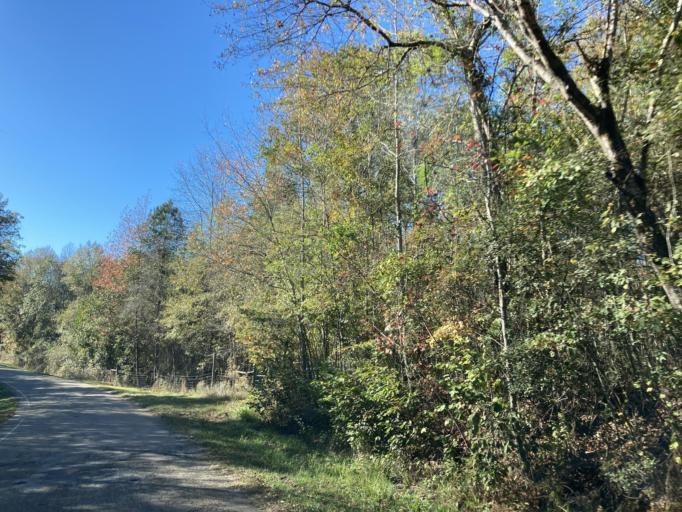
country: US
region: Mississippi
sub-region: Lamar County
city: Sumrall
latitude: 31.2981
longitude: -89.6434
